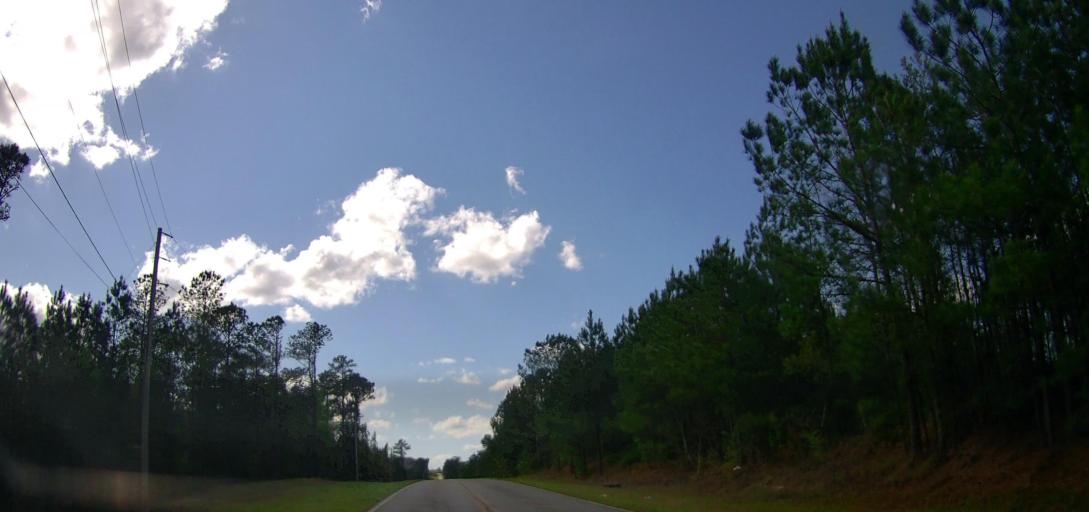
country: US
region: Georgia
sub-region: Wilkinson County
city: Gordon
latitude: 32.8014
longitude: -83.4239
